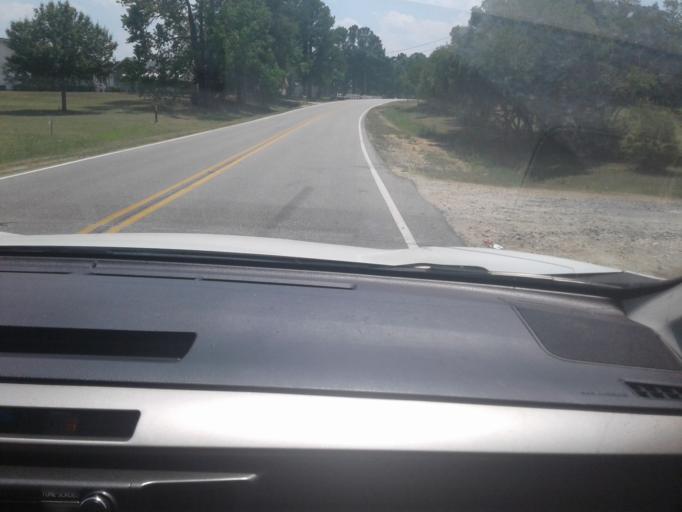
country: US
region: North Carolina
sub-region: Johnston County
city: Benson
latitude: 35.3971
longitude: -78.6016
